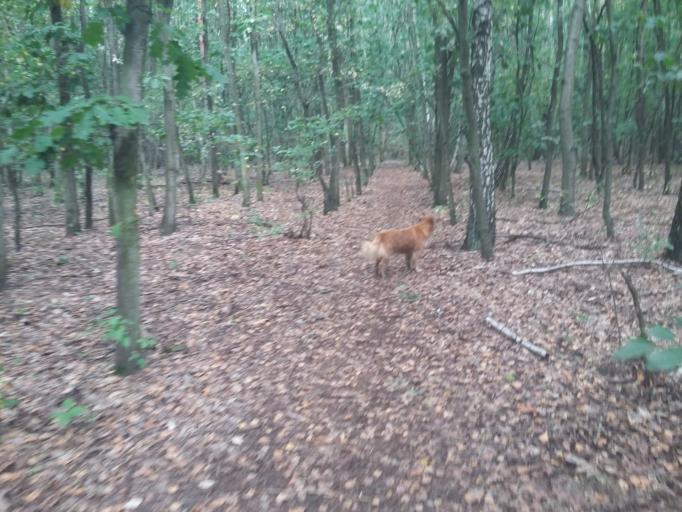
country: PL
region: Lodz Voivodeship
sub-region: Powiat pabianicki
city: Ksawerow
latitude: 51.7272
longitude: 19.3904
